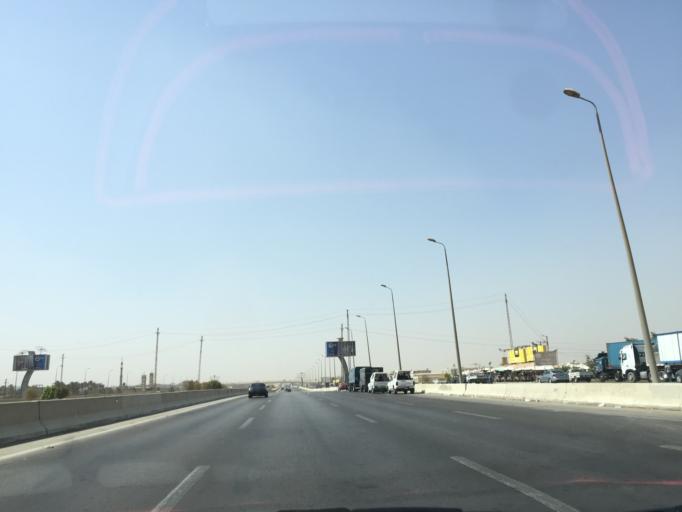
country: EG
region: Al Jizah
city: Awsim
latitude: 30.0733
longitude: 31.0088
